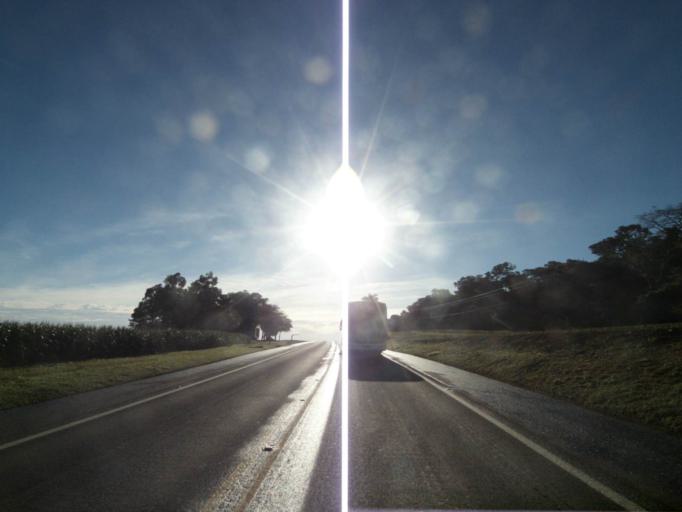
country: BR
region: Parana
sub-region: Matelandia
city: Matelandia
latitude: -25.1119
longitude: -53.7682
